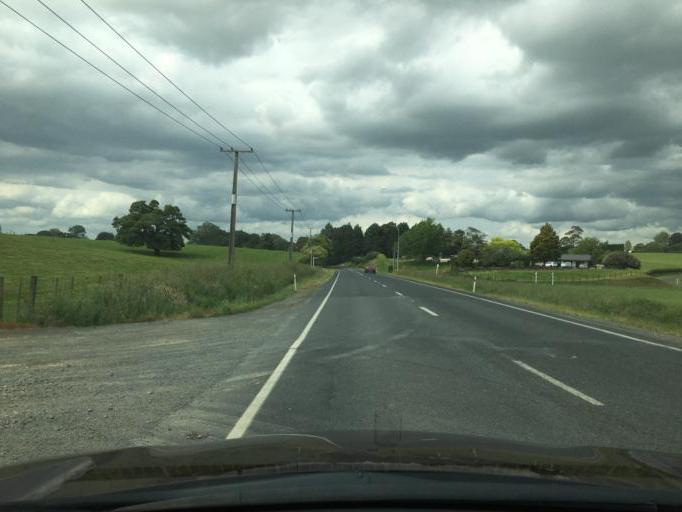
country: NZ
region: Waikato
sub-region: Waipa District
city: Cambridge
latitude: -38.0144
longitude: 175.3654
